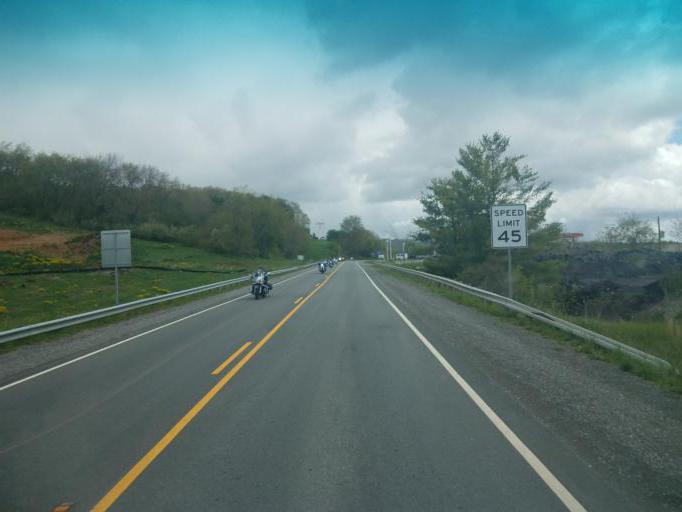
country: US
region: Virginia
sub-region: Bland County
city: Bland
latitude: 37.0984
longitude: -81.1332
